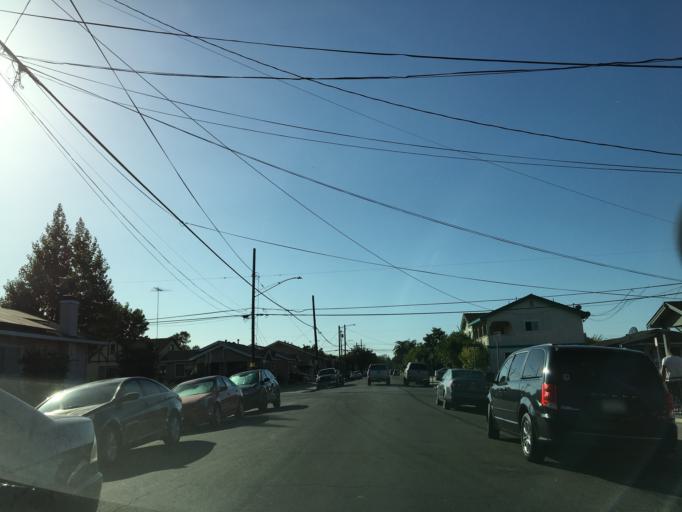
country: US
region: California
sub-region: Santa Clara County
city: Alum Rock
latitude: 37.3506
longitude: -121.8586
